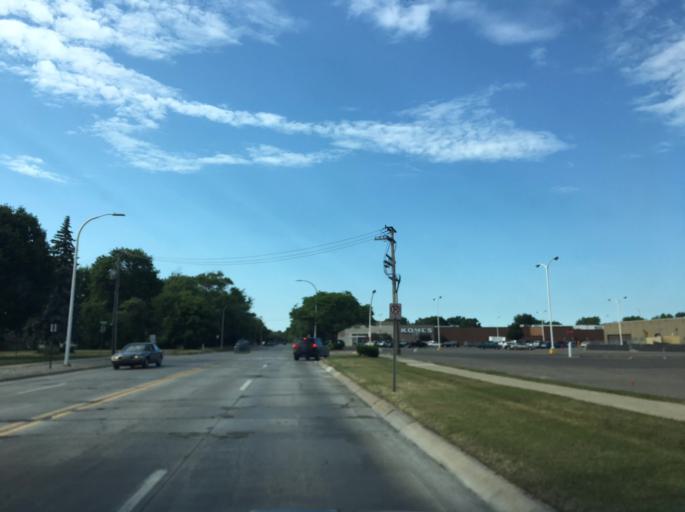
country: US
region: Michigan
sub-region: Macomb County
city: Fraser
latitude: 42.5329
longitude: -82.9192
